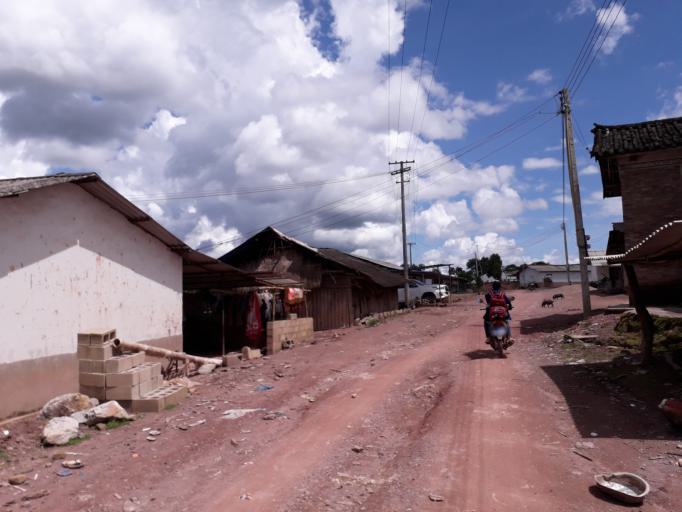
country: CN
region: Yunnan
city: Menglie
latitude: 22.2651
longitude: 101.5745
